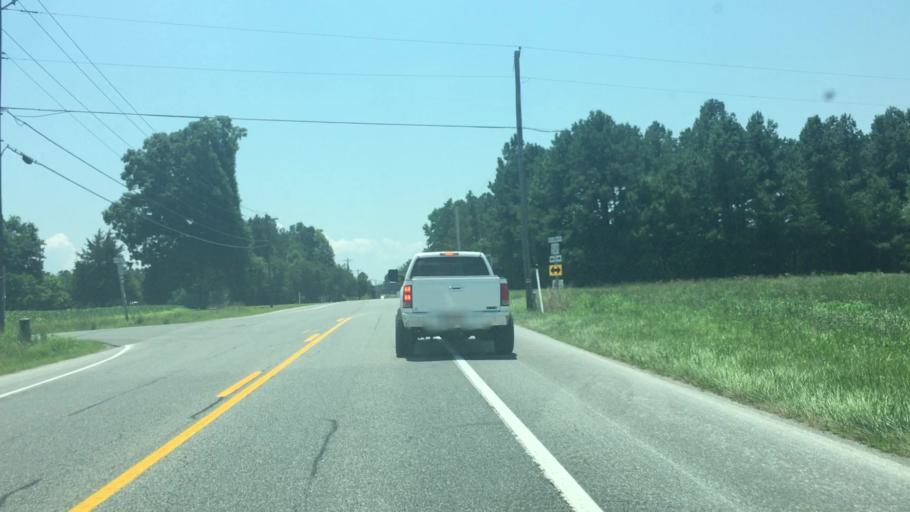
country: US
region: Maryland
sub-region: Saint Mary's County
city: Leonardtown
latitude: 38.3739
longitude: -76.6785
